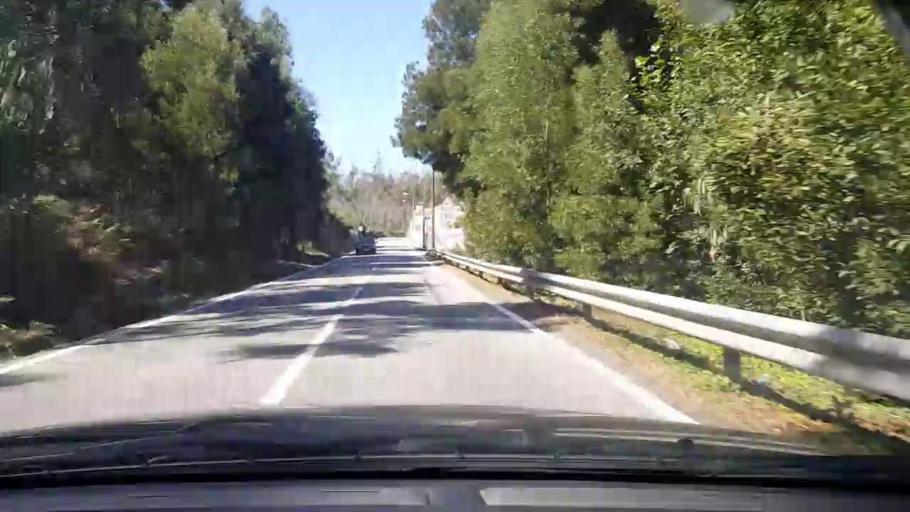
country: PT
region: Porto
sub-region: Vila do Conde
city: Arvore
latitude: 41.3416
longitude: -8.6535
